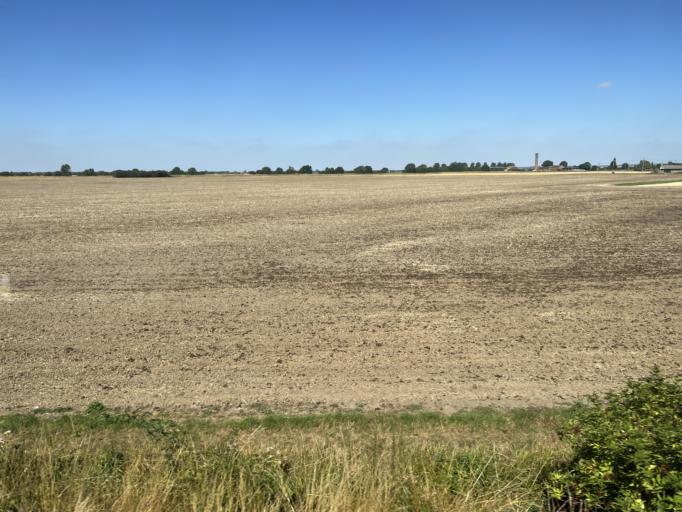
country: GB
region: England
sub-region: Lincolnshire
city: Spilsby
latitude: 53.0634
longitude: 0.0628
